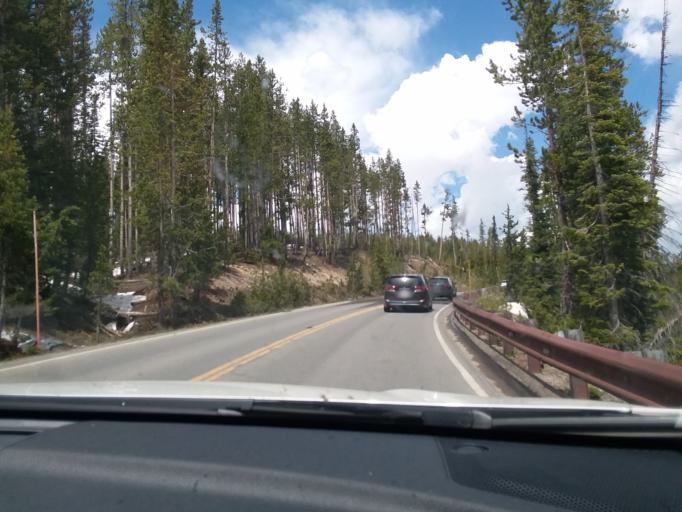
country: US
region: Montana
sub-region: Gallatin County
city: West Yellowstone
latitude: 44.2045
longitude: -110.6606
